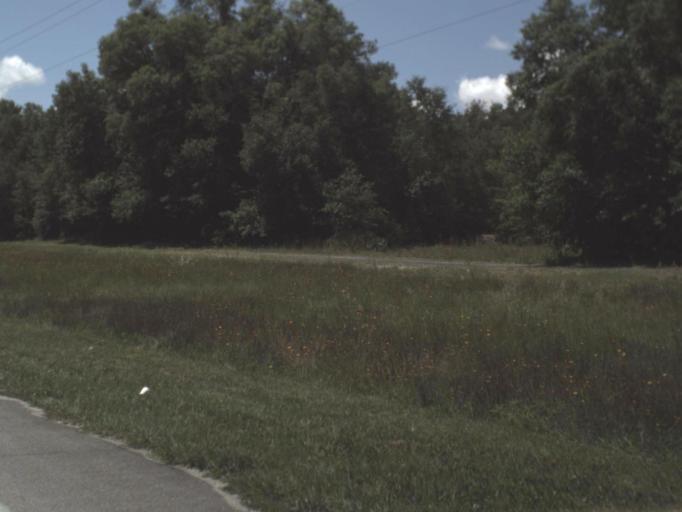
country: US
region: Florida
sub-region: Putnam County
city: Palatka
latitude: 29.5156
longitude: -81.6157
